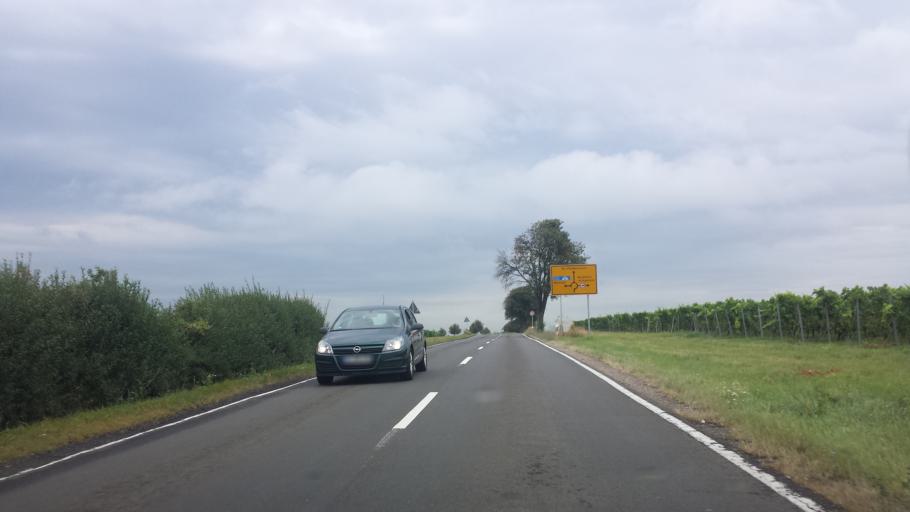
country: DE
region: Rheinland-Pfalz
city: Morstadt
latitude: 49.6512
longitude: 8.2362
